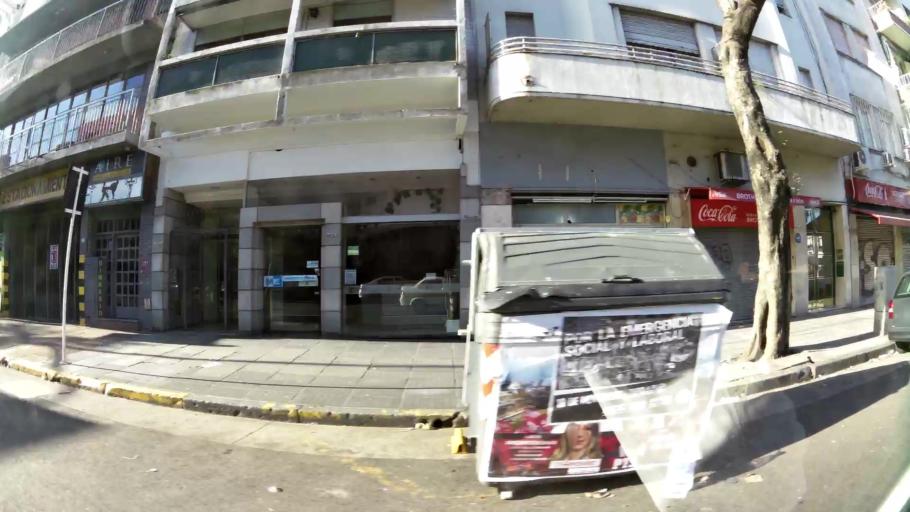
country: AR
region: Buenos Aires F.D.
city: Buenos Aires
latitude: -34.6130
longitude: -58.3823
